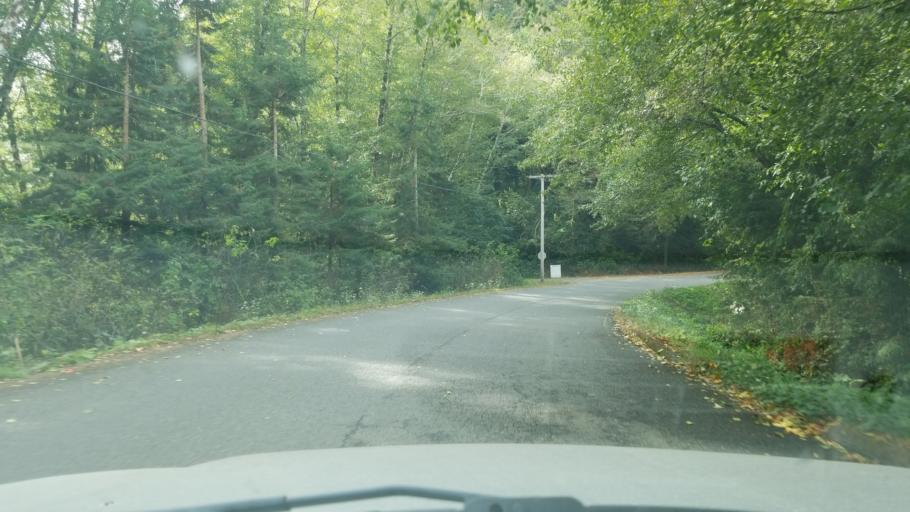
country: US
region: California
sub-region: Del Norte County
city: Bertsch-Oceanview
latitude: 41.5119
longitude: -124.0364
